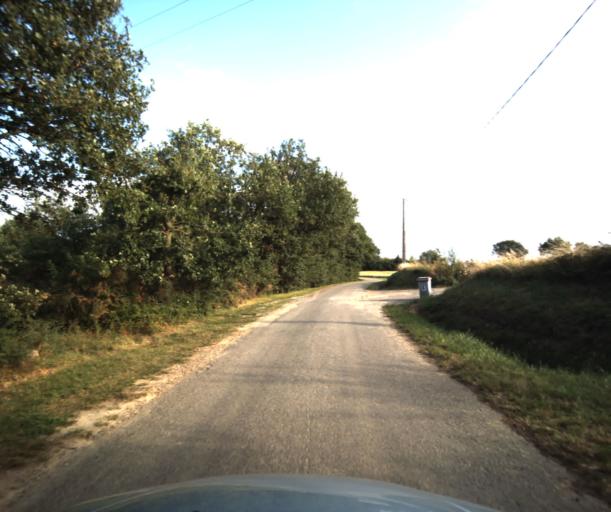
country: FR
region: Midi-Pyrenees
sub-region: Departement de la Haute-Garonne
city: Eaunes
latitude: 43.4342
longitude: 1.3339
